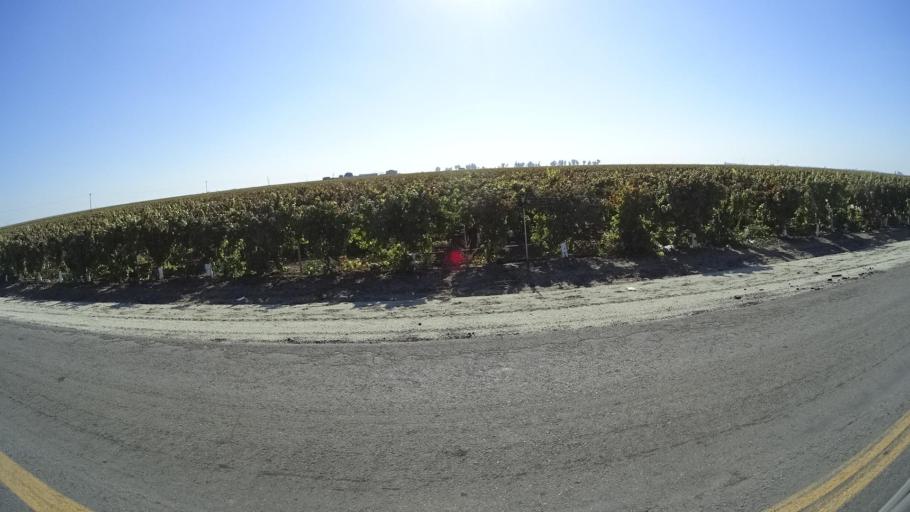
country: US
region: California
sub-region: Kern County
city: McFarland
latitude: 35.7034
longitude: -119.1889
